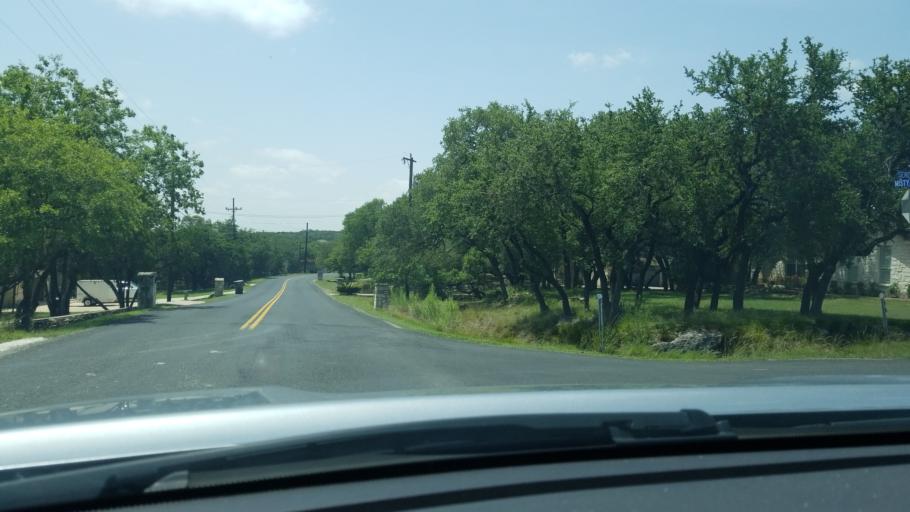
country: US
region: Texas
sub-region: Bexar County
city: Timberwood Park
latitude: 29.6925
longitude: -98.4803
